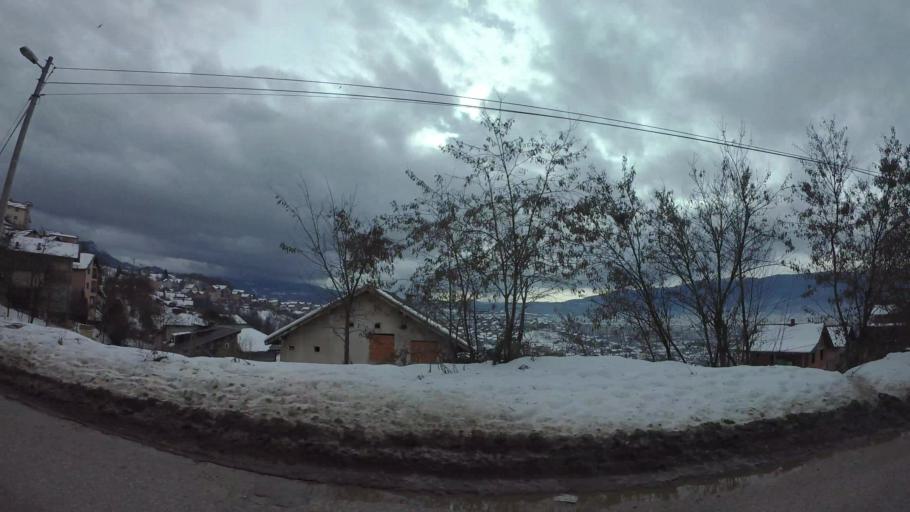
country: BA
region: Federation of Bosnia and Herzegovina
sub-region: Kanton Sarajevo
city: Sarajevo
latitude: 43.8640
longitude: 18.3497
